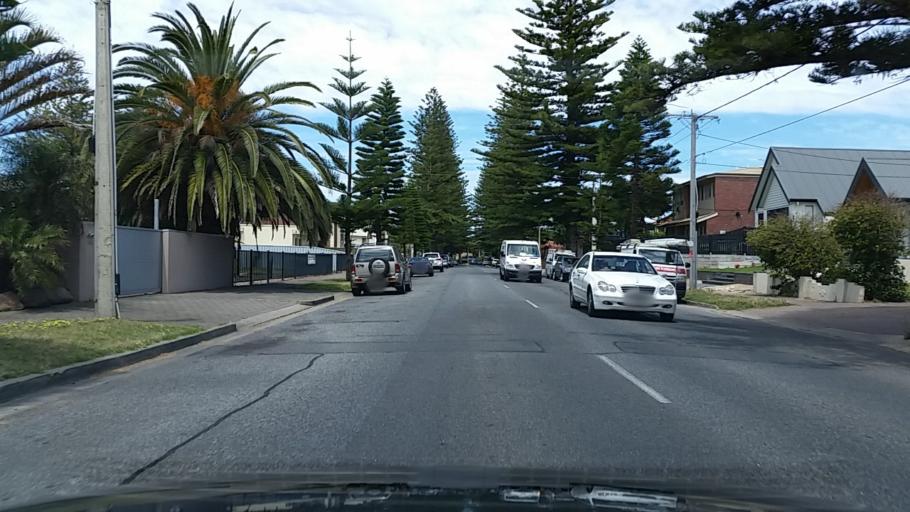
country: AU
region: South Australia
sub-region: Charles Sturt
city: Henley Beach
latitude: -34.9228
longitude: 138.4967
